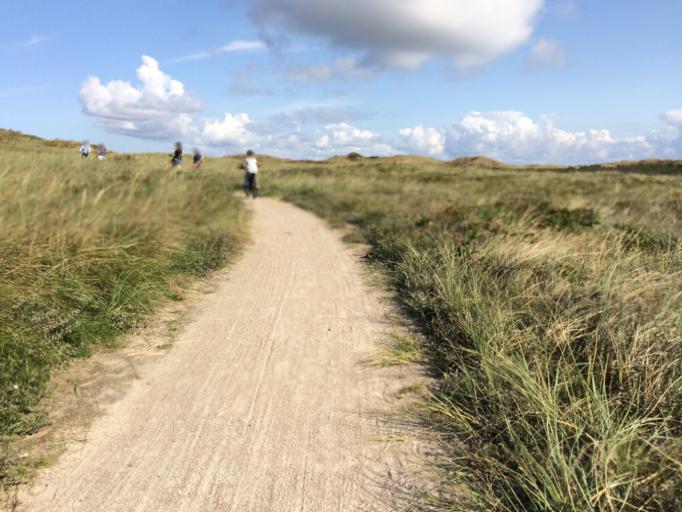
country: DK
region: Central Jutland
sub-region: Ringkobing-Skjern Kommune
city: Hvide Sande
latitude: 55.9335
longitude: 8.1504
